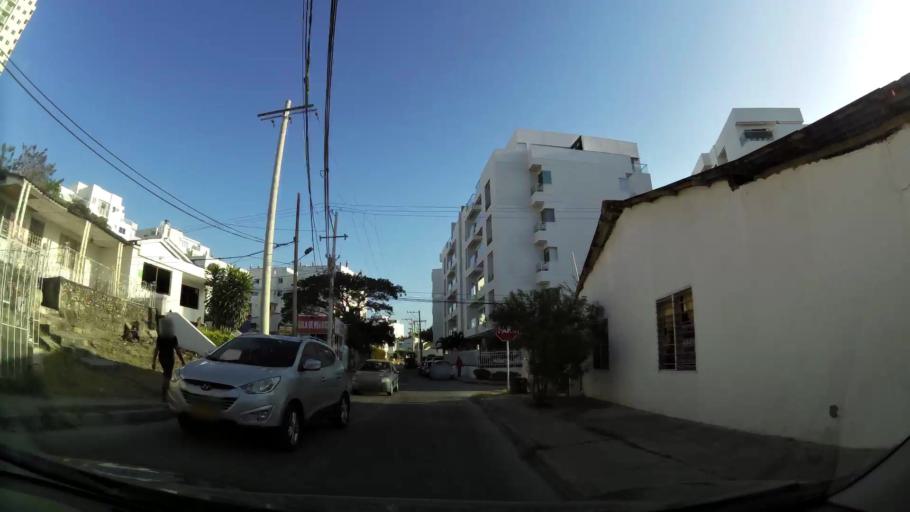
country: CO
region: Bolivar
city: Cartagena
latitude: 10.3951
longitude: -75.5198
